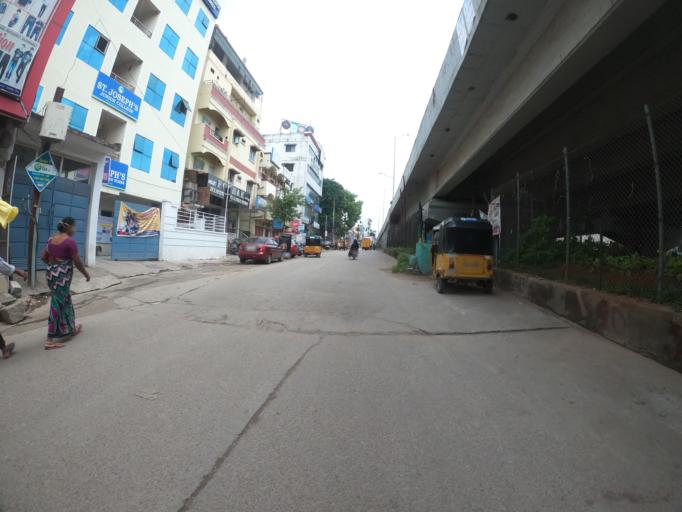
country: IN
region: Telangana
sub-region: Hyderabad
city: Hyderabad
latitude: 17.3996
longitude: 78.4145
